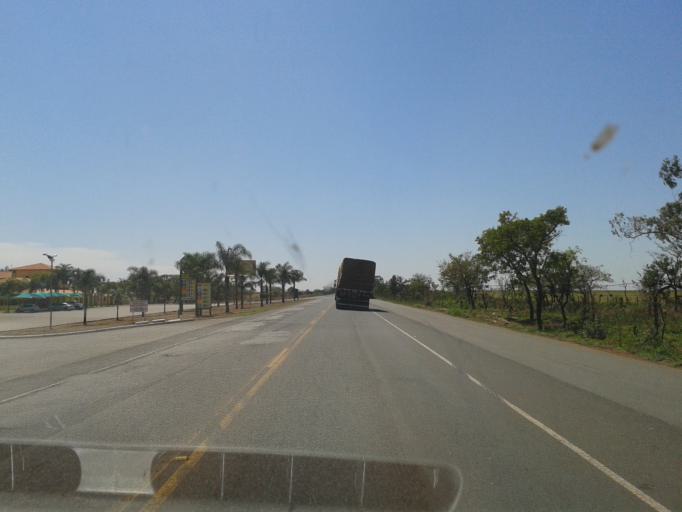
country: BR
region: Minas Gerais
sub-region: Monte Carmelo
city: Monte Carmelo
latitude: -19.2950
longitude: -47.4841
